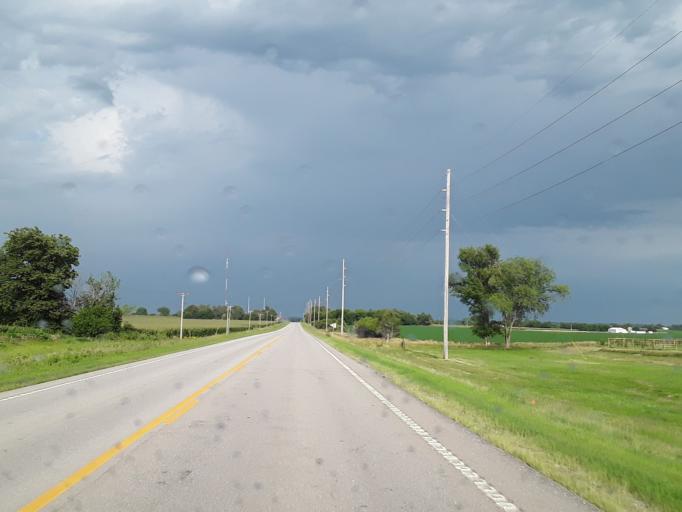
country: US
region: Nebraska
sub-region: Saunders County
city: Ashland
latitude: 41.0887
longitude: -96.3985
